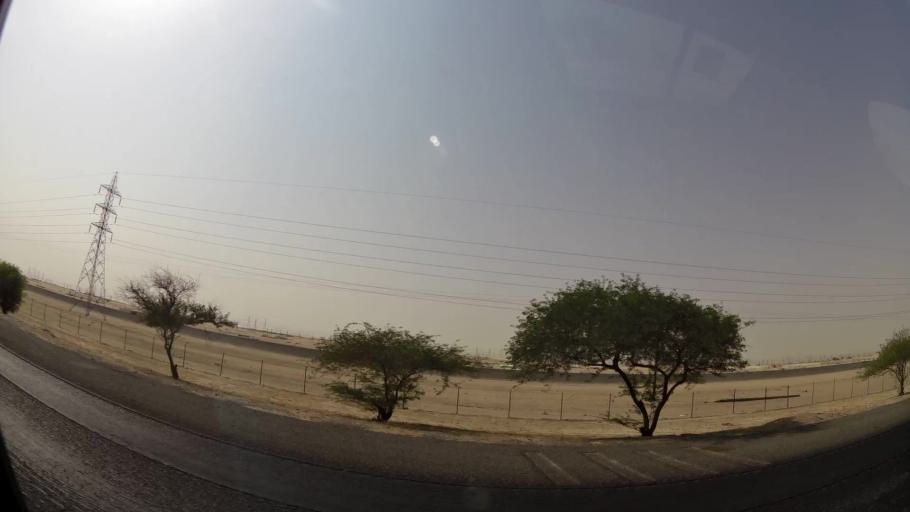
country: KW
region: Muhafazat al Jahra'
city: Al Jahra'
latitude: 29.3186
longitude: 47.6447
